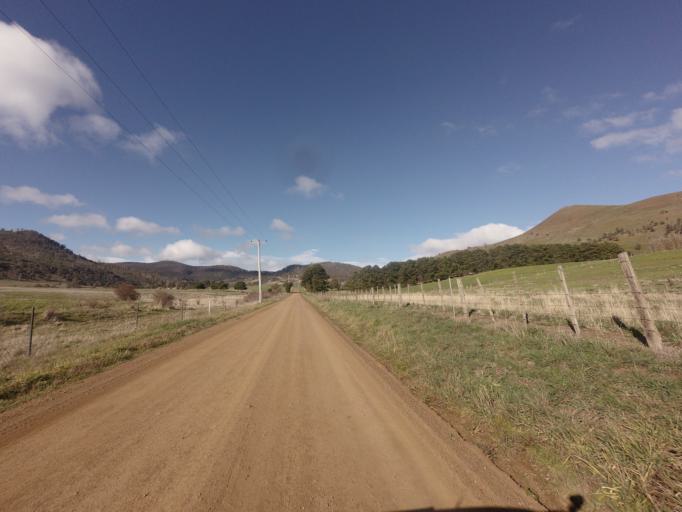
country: AU
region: Tasmania
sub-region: Derwent Valley
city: New Norfolk
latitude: -42.6978
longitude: 146.9753
